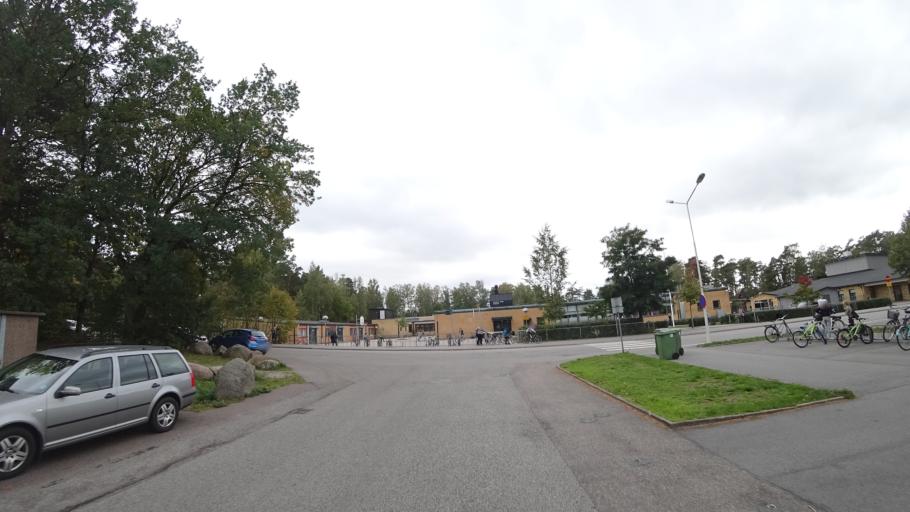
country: SE
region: Skane
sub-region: Kavlinge Kommun
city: Kaevlinge
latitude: 55.7757
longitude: 13.0854
